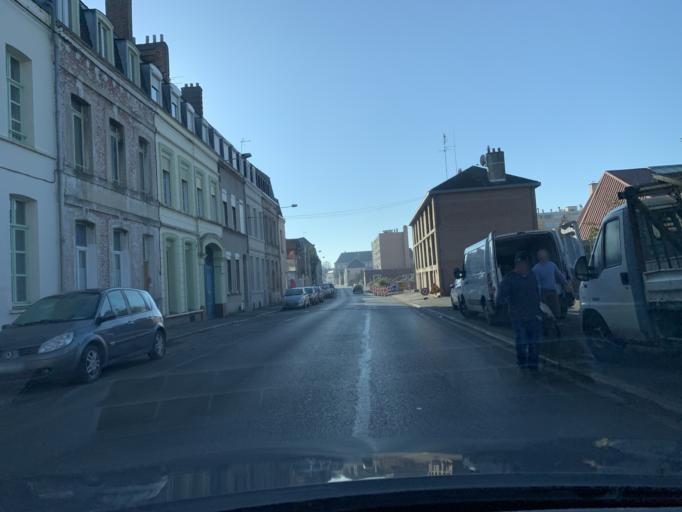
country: FR
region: Nord-Pas-de-Calais
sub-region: Departement du Nord
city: Neuville-Saint-Remy
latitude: 50.1806
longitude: 3.2300
